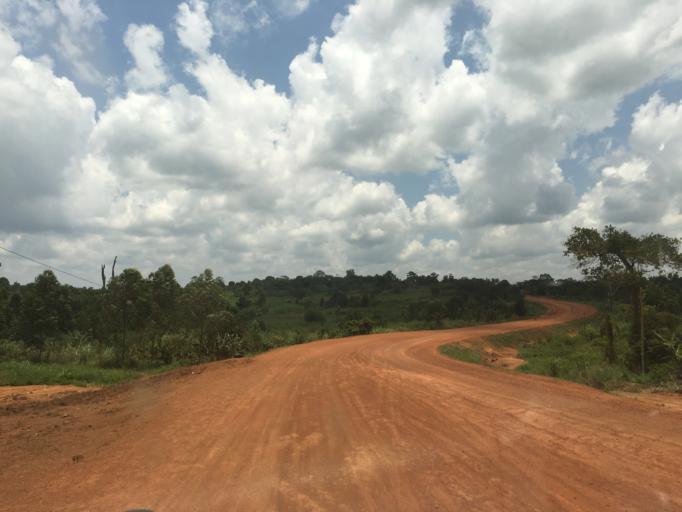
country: UG
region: Western Region
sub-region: Kibale District
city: Kagadi
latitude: 1.1702
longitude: 31.0280
